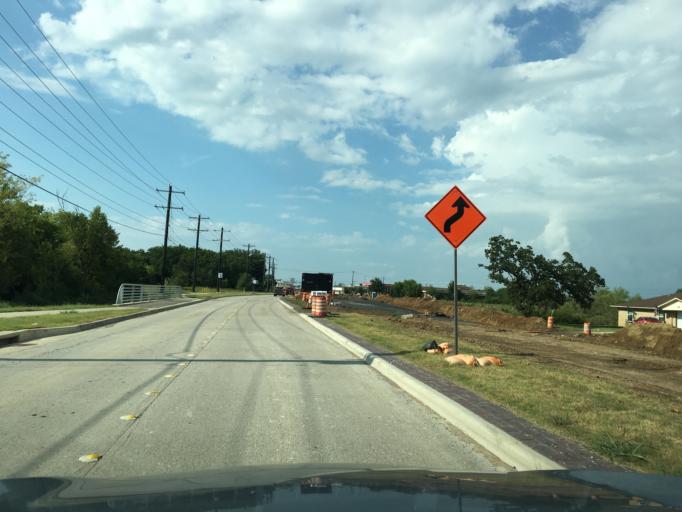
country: US
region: Texas
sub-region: Denton County
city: Denton
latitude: 33.2310
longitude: -97.0828
